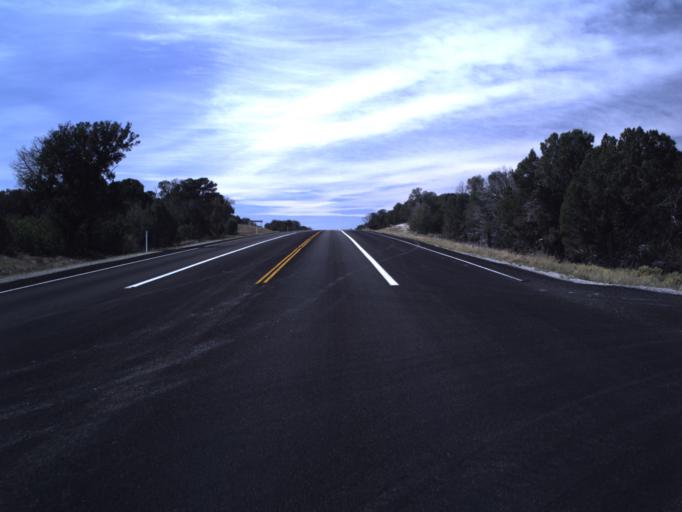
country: US
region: Colorado
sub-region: Dolores County
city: Dove Creek
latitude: 37.8382
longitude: -109.1176
